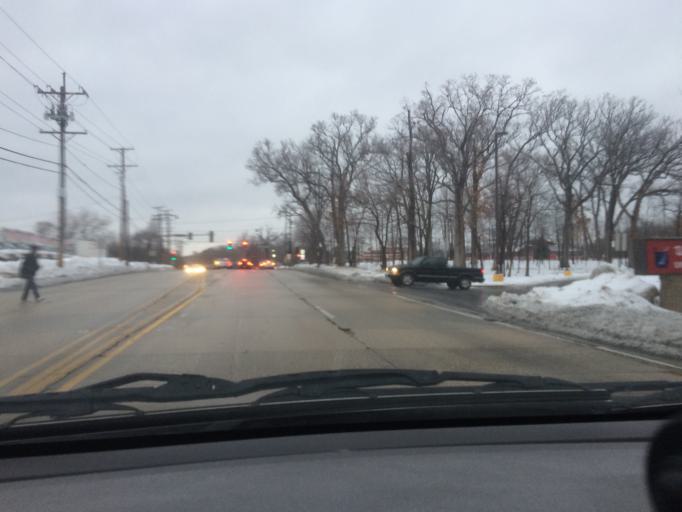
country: US
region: Illinois
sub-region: Cook County
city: Streamwood
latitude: 42.0124
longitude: -88.1836
